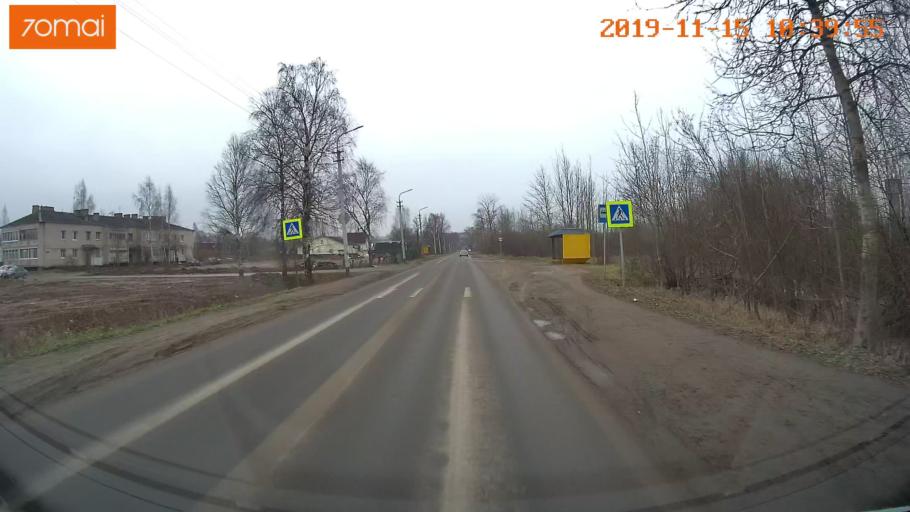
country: RU
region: Vologda
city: Sheksna
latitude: 59.2182
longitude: 38.5108
